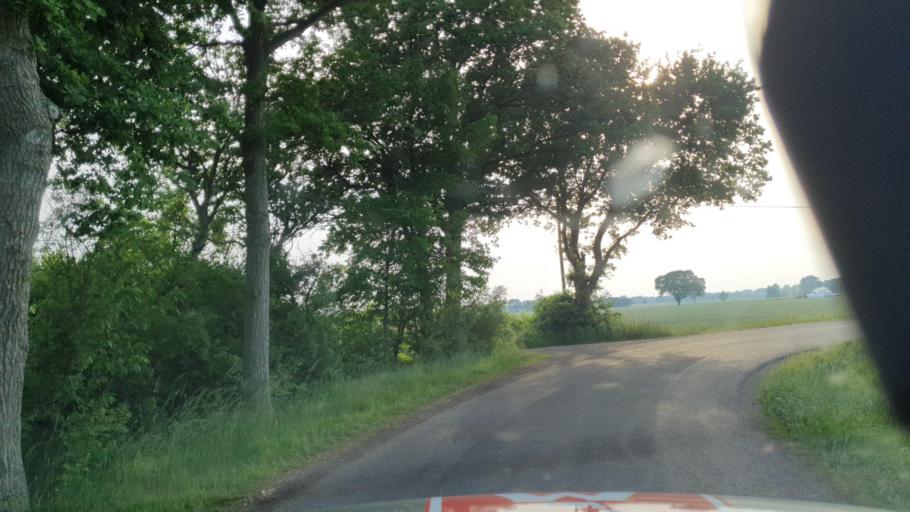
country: SE
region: Kalmar
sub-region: Kalmar Kommun
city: Ljungbyholm
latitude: 56.5638
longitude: 16.1545
